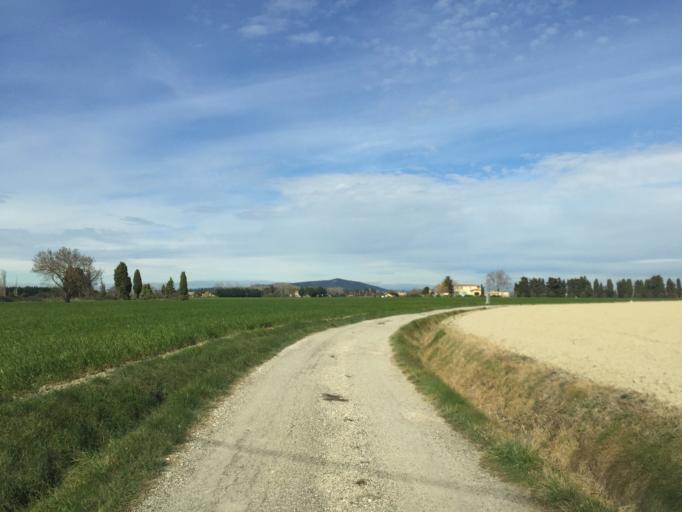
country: FR
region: Provence-Alpes-Cote d'Azur
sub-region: Departement du Vaucluse
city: Caderousse
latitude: 44.1110
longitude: 4.7513
